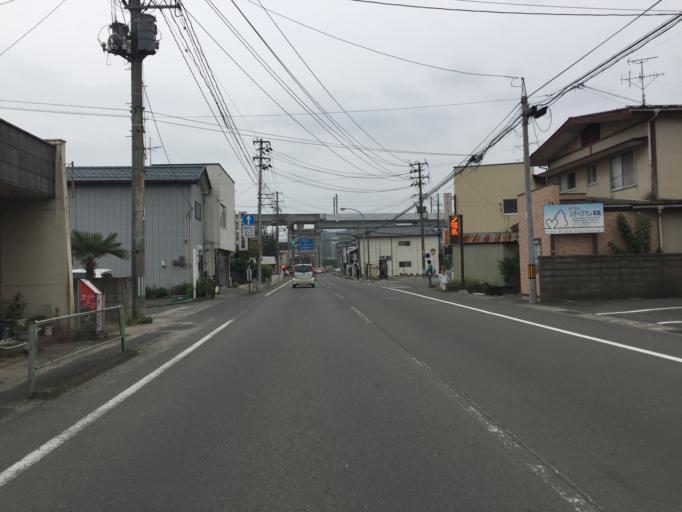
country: JP
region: Fukushima
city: Fukushima-shi
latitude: 37.7439
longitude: 140.4560
